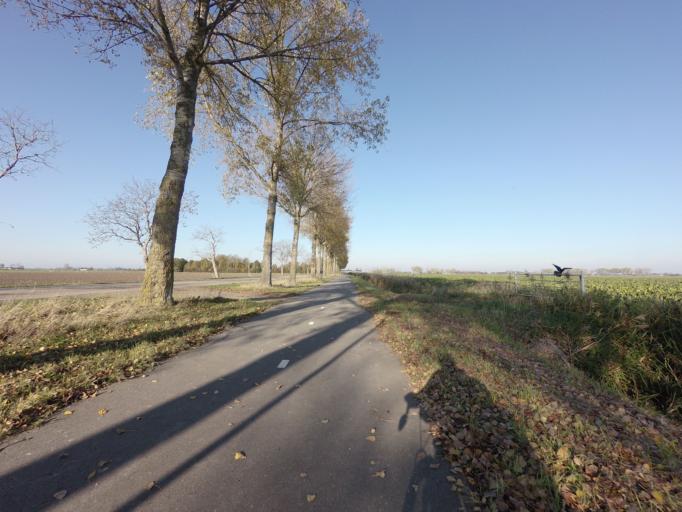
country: NL
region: North Brabant
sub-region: Gemeente Waalwijk
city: Waalwijk
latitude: 51.7216
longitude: 5.0567
